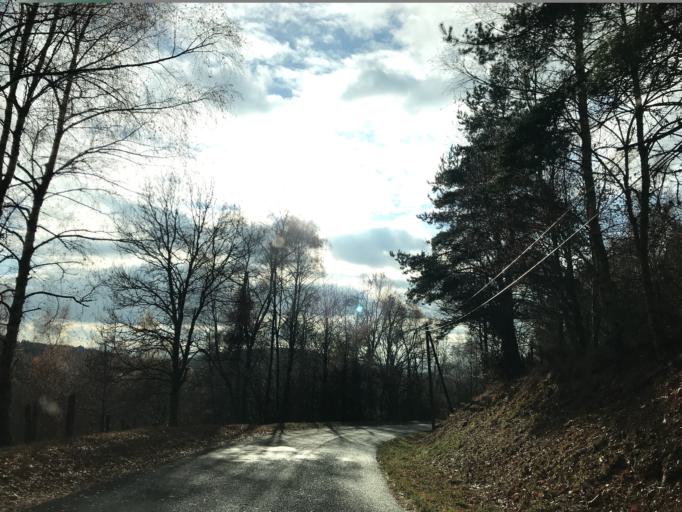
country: FR
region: Auvergne
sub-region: Departement du Puy-de-Dome
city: Celles-sur-Durolle
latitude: 45.7758
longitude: 3.6681
